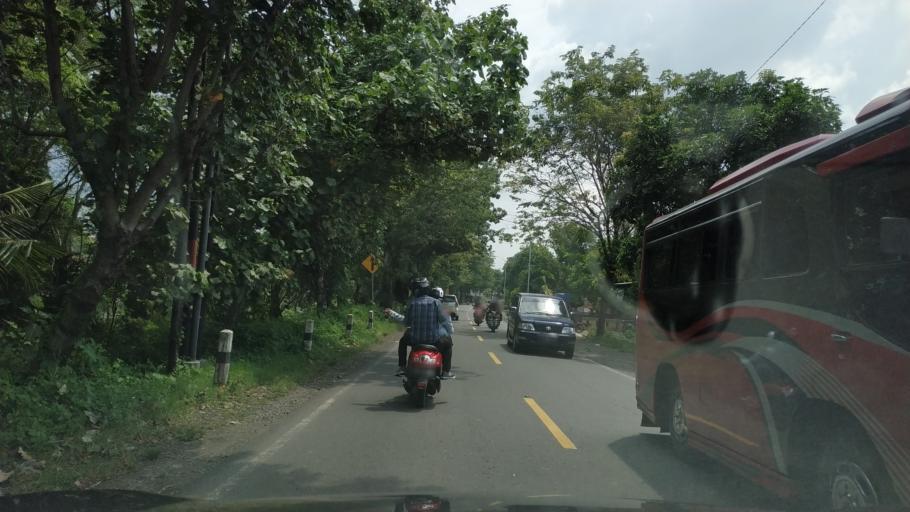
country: ID
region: Central Java
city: Lebaksiu
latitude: -7.0236
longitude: 109.1423
